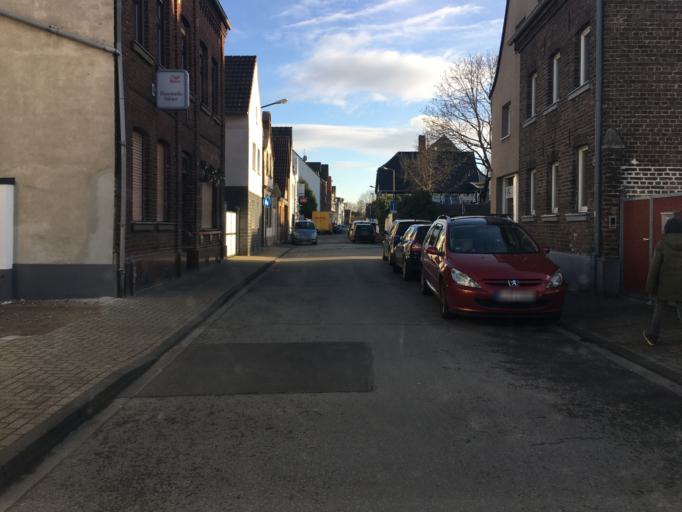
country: DE
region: North Rhine-Westphalia
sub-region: Regierungsbezirk Koln
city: Porz am Rhein
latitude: 50.8746
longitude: 7.0317
